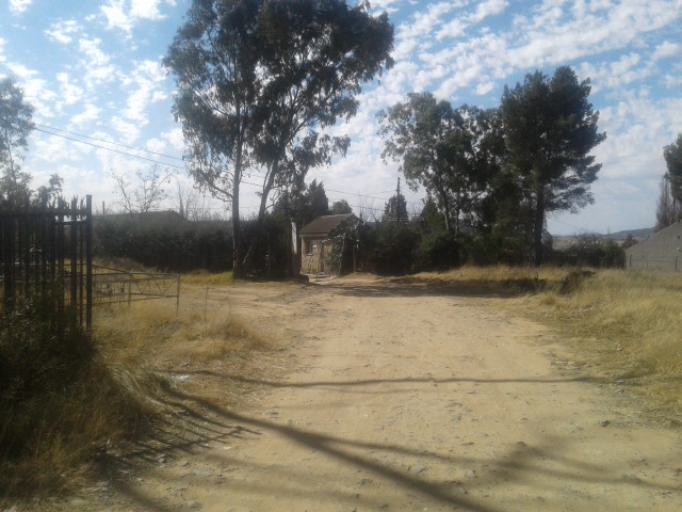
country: LS
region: Maseru
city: Maseru
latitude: -29.3064
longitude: 27.4779
